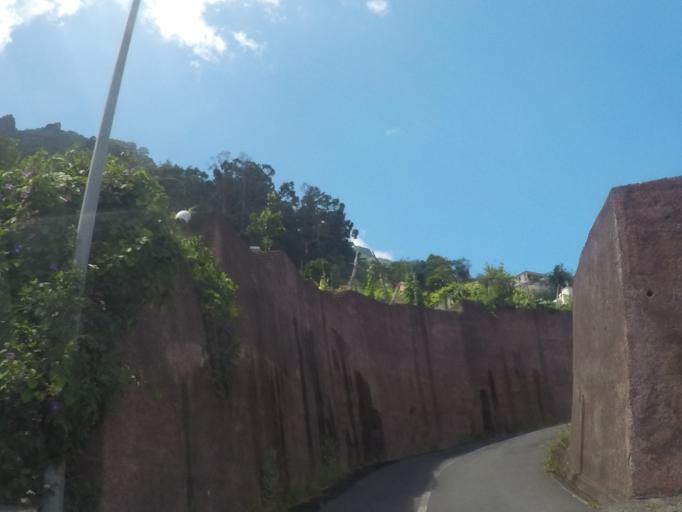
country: PT
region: Madeira
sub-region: Camara de Lobos
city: Curral das Freiras
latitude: 32.7074
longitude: -16.9736
